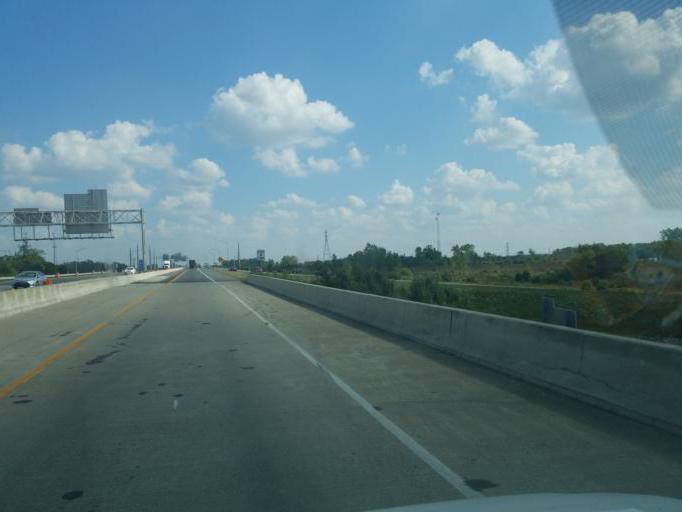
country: US
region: Indiana
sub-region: Allen County
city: Fort Wayne
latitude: 41.1683
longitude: -85.1045
